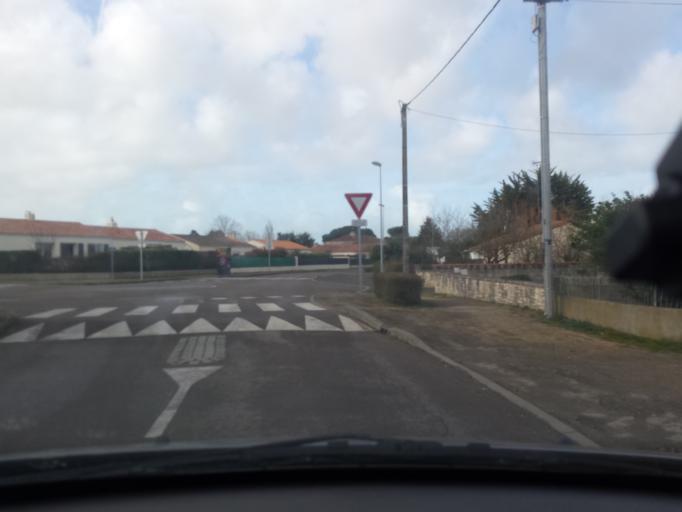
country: FR
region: Pays de la Loire
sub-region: Departement de la Vendee
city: Olonne-sur-Mer
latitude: 46.5628
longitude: -1.7760
